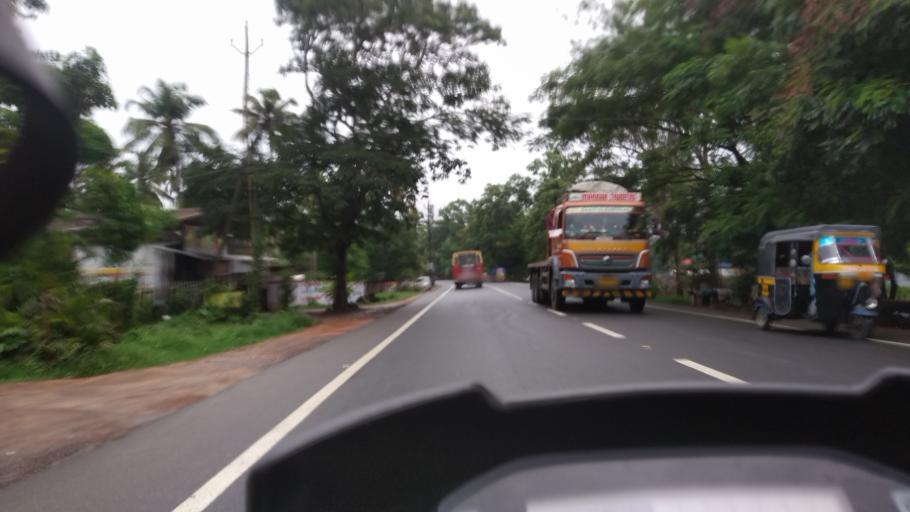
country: IN
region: Kerala
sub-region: Alappuzha
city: Mavelikara
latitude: 9.2864
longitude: 76.4392
